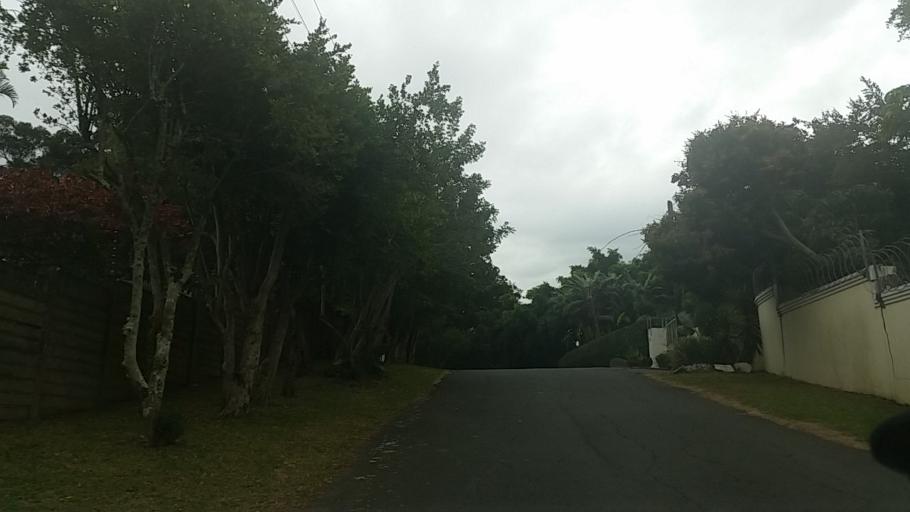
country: ZA
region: KwaZulu-Natal
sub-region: eThekwini Metropolitan Municipality
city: Berea
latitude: -29.8411
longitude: 30.9417
